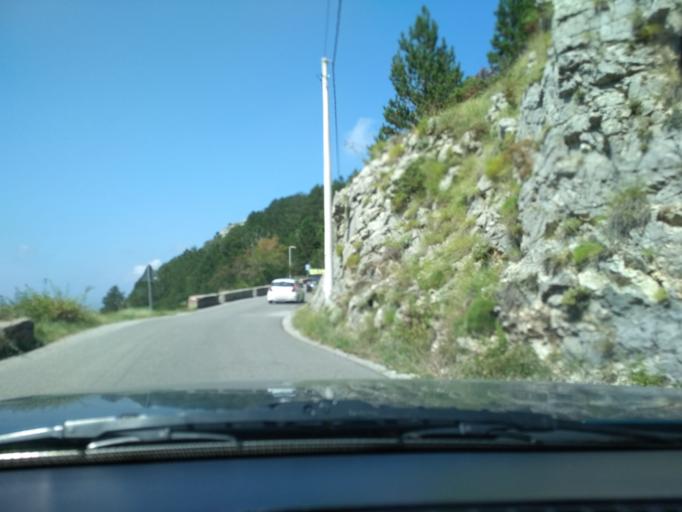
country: ME
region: Kotor
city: Kotor
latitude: 42.4241
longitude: 18.8005
